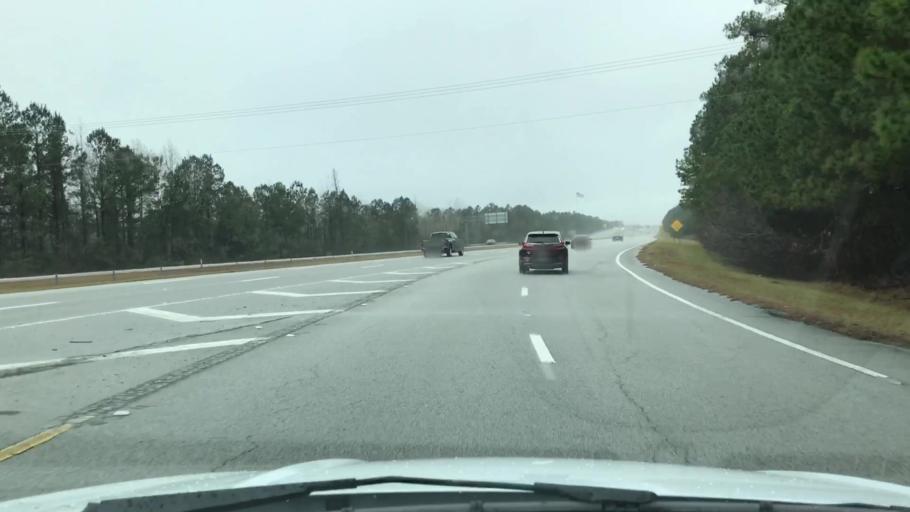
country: US
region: South Carolina
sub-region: Horry County
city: Myrtle Beach
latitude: 33.7527
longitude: -78.8594
